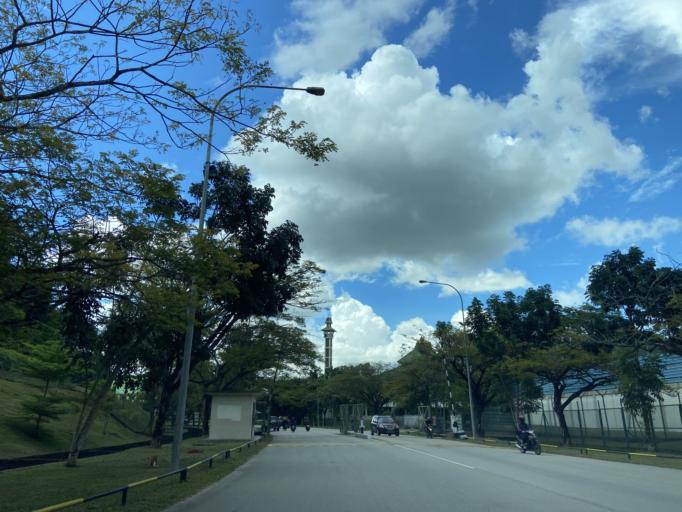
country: SG
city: Singapore
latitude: 1.0648
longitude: 104.0249
